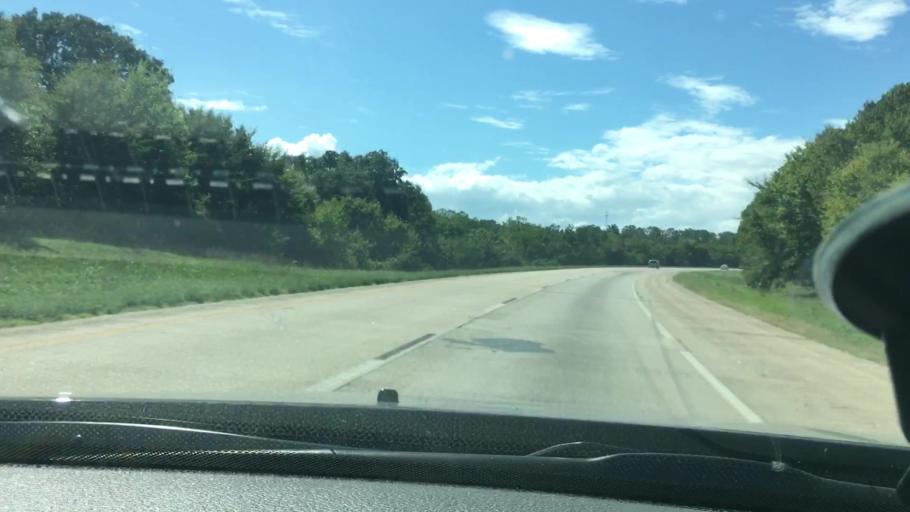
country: US
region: Oklahoma
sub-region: Sequoyah County
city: Vian
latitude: 35.4900
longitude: -94.9936
